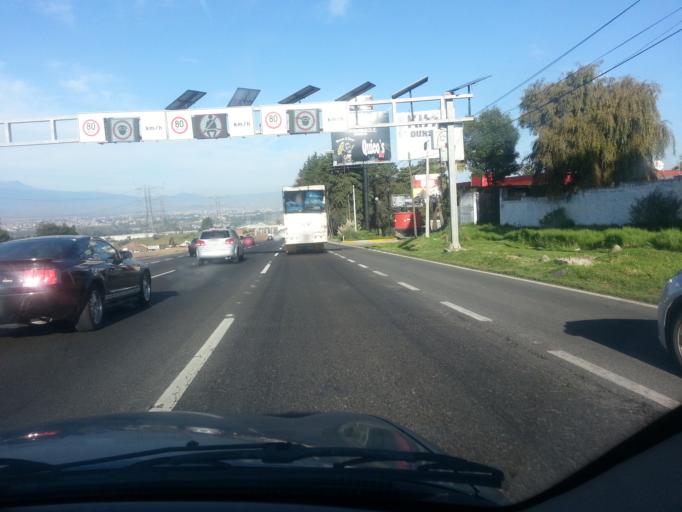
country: MX
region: Mexico
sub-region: Lerma
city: Fraccionamiento y Club de Golf los Encinos
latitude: 19.2829
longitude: -99.4748
